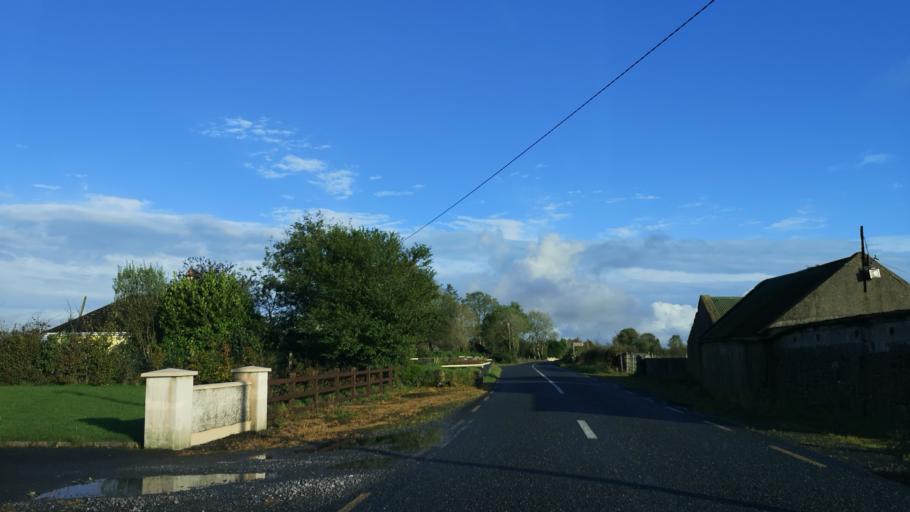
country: IE
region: Connaught
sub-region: Roscommon
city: Castlerea
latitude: 53.8086
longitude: -8.5166
